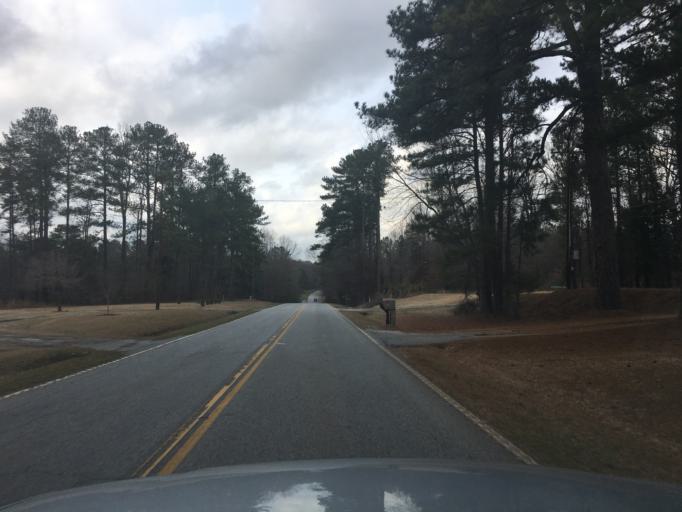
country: US
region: South Carolina
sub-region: Abbeville County
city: Abbeville
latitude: 34.2107
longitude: -82.3888
